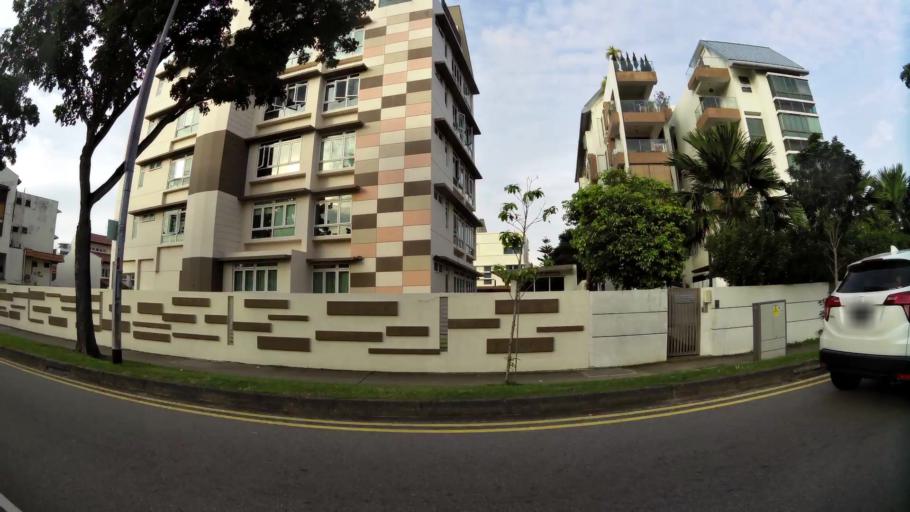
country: SG
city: Singapore
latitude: 1.3163
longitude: 103.9054
